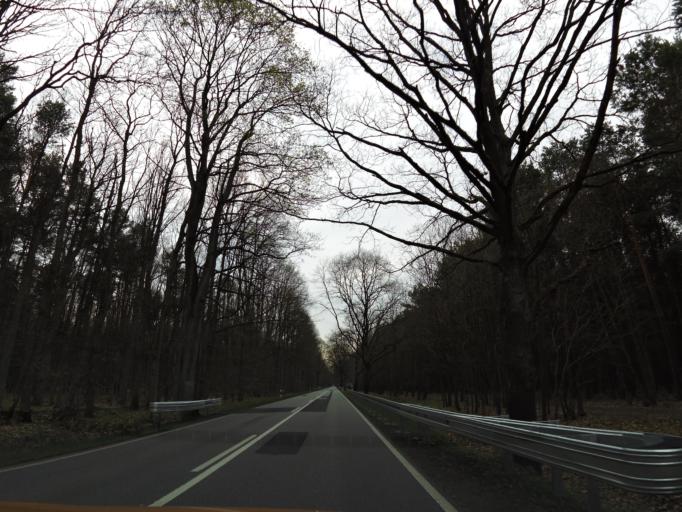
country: DE
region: Brandenburg
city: Mixdorf
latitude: 52.2314
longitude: 14.3732
